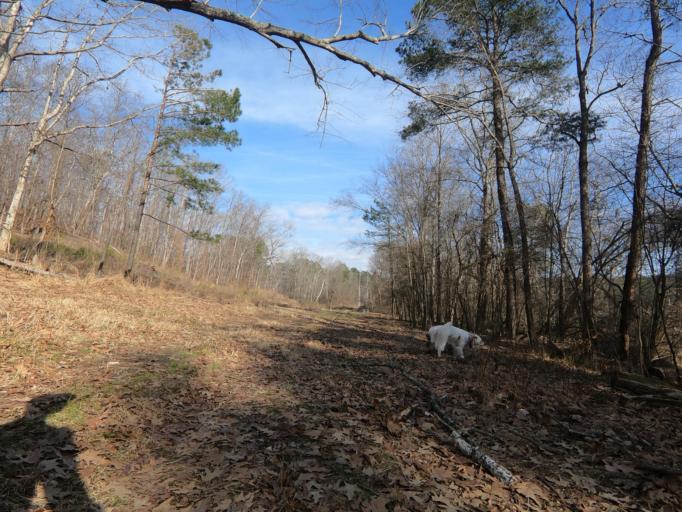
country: US
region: Georgia
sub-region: Cobb County
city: Acworth
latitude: 34.0522
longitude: -84.6578
